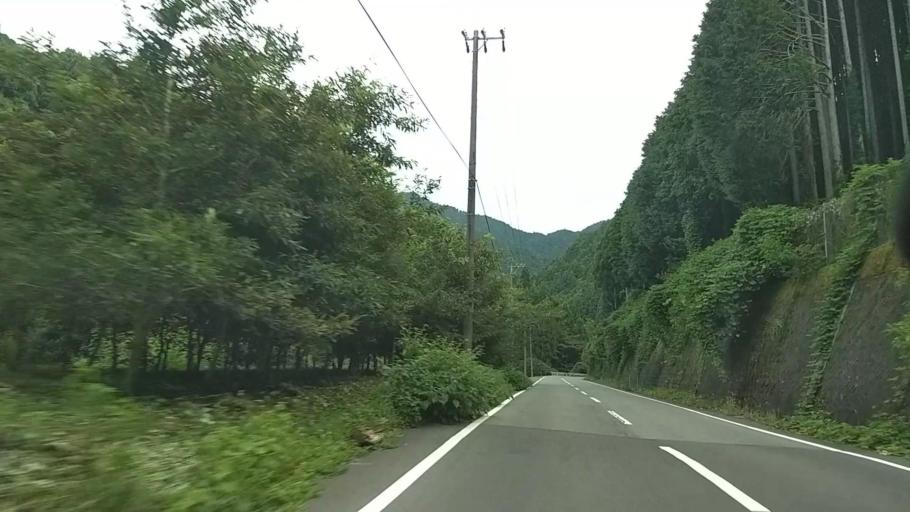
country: JP
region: Shizuoka
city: Fujinomiya
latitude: 35.1639
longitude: 138.5386
